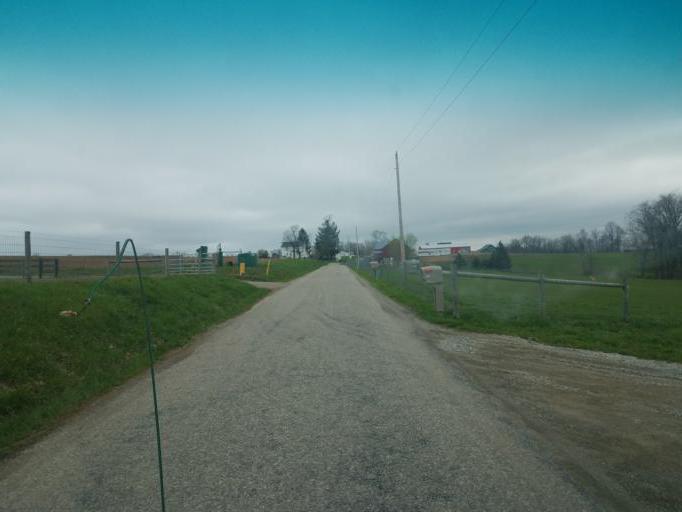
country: US
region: Ohio
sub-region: Stark County
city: Beach City
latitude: 40.6343
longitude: -81.6540
